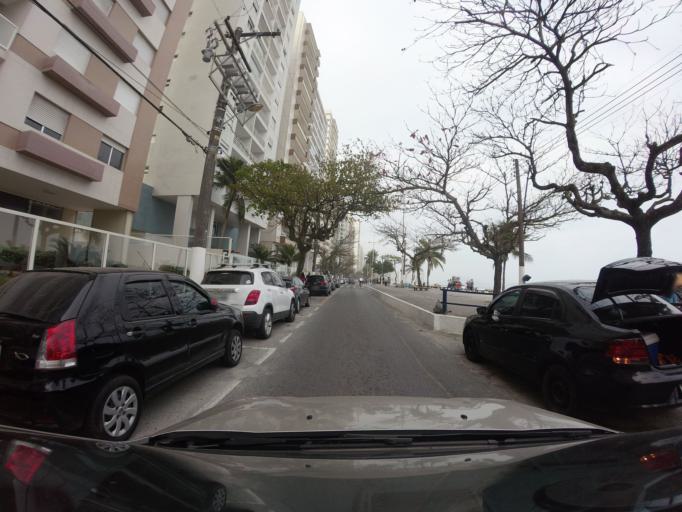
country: BR
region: Sao Paulo
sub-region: Guaruja
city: Guaruja
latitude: -24.0014
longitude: -46.2646
